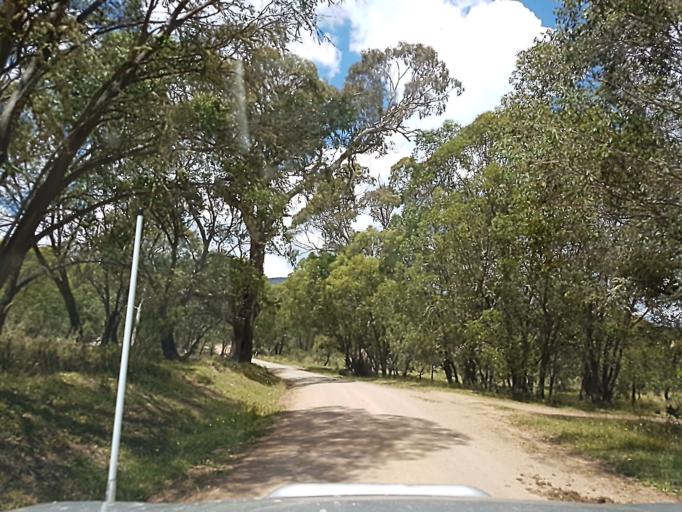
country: AU
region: New South Wales
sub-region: Snowy River
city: Jindabyne
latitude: -36.8961
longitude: 148.0902
